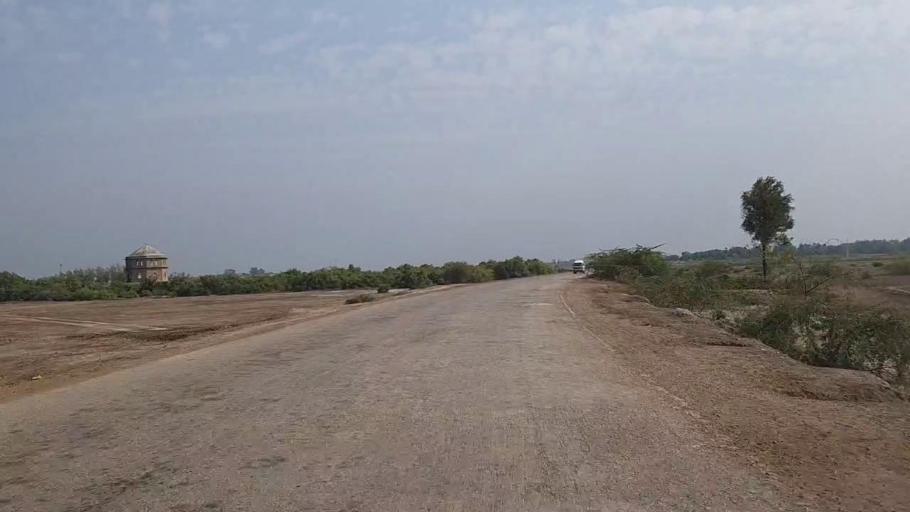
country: PK
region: Sindh
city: Mirwah Gorchani
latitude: 25.4151
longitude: 69.0336
